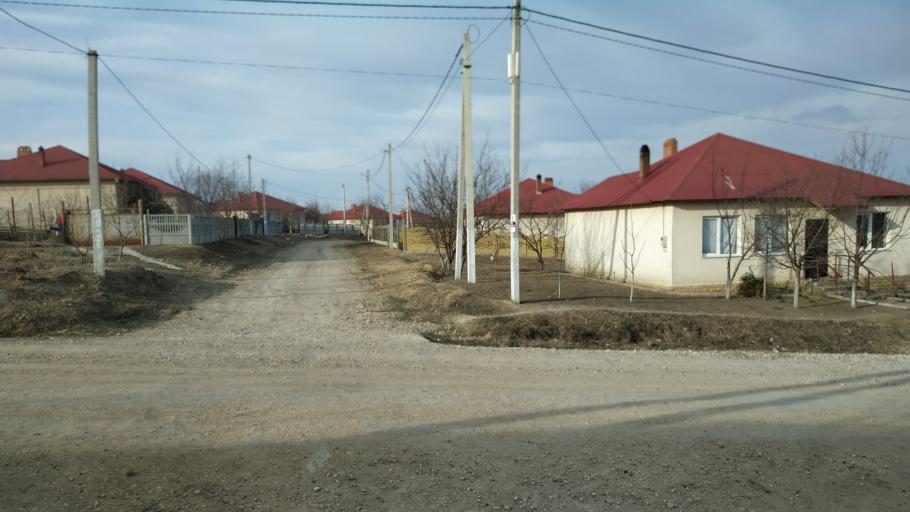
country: RO
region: Vaslui
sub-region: Comuna Dranceni
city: Dranceni
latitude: 46.8434
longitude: 28.1858
